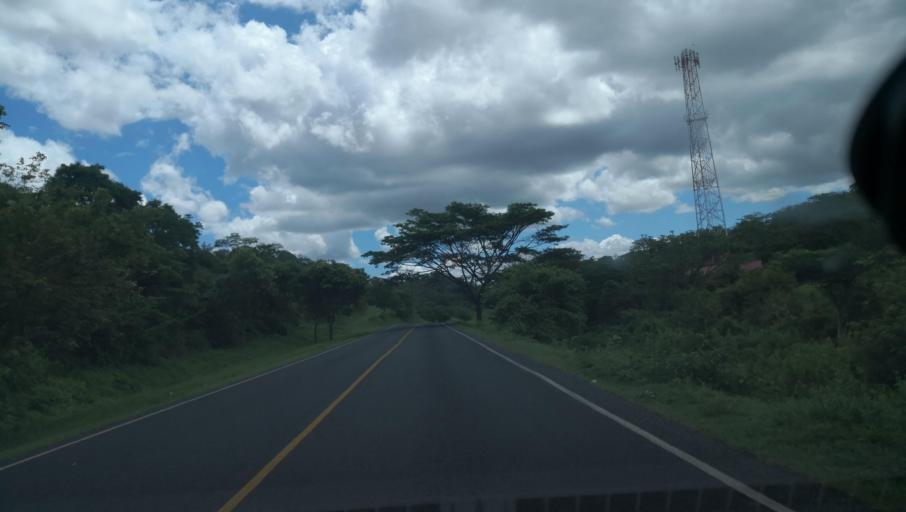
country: NI
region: Madriz
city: Palacaguina
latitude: 13.4438
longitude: -86.4390
